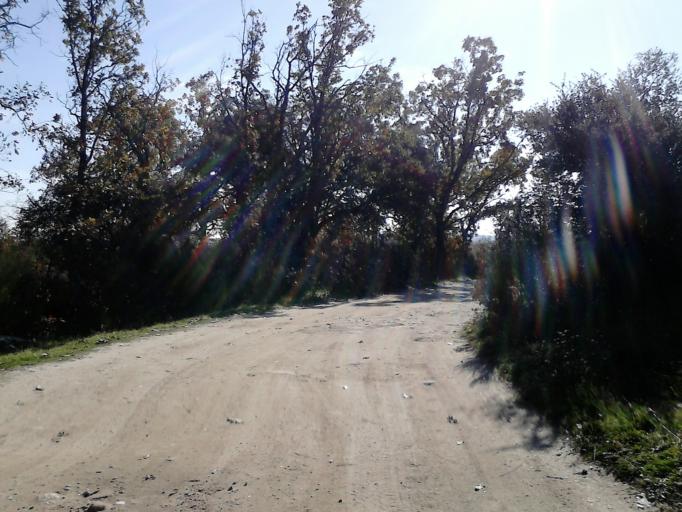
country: ES
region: Madrid
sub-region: Provincia de Madrid
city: El Escorial
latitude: 40.5954
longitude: -4.1108
